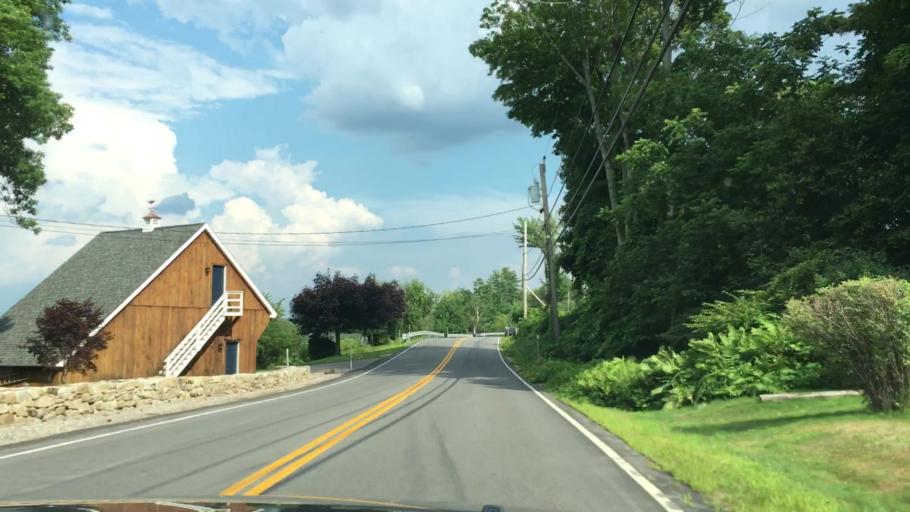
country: US
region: New Hampshire
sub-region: Belknap County
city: Gilford
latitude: 43.5614
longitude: -71.3332
